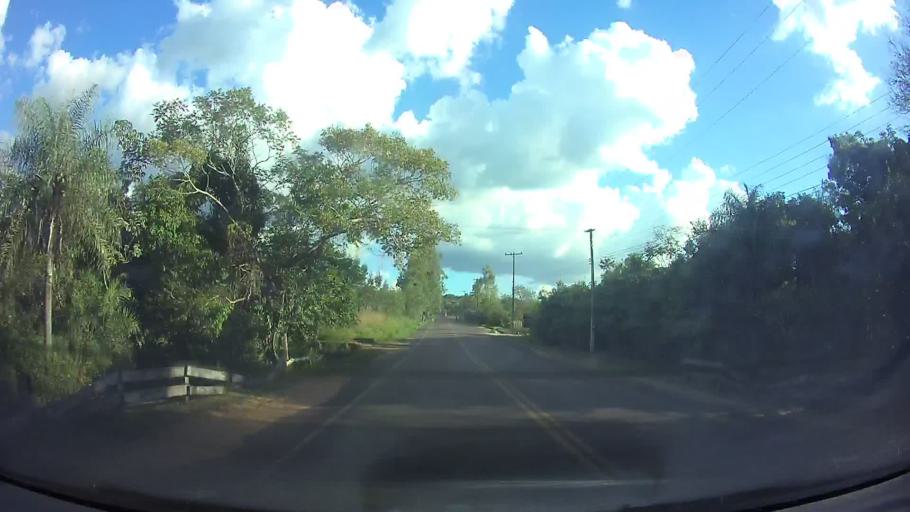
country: PY
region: Cordillera
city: Altos
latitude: -25.1902
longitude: -57.2243
